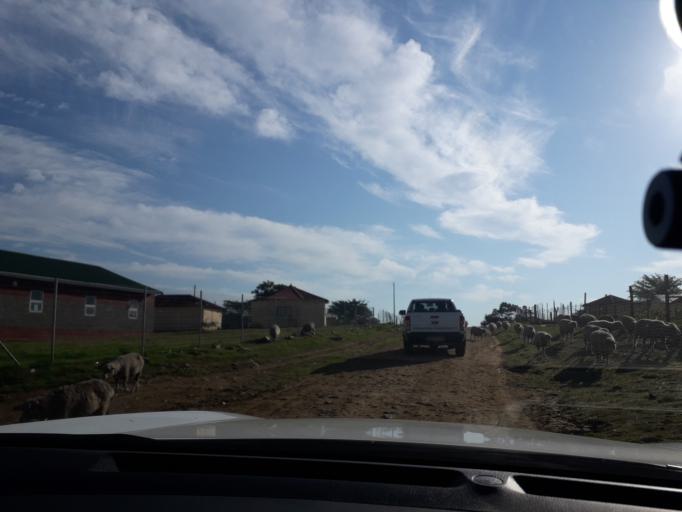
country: ZA
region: Eastern Cape
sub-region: Buffalo City Metropolitan Municipality
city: Bhisho
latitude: -32.9382
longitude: 27.2902
